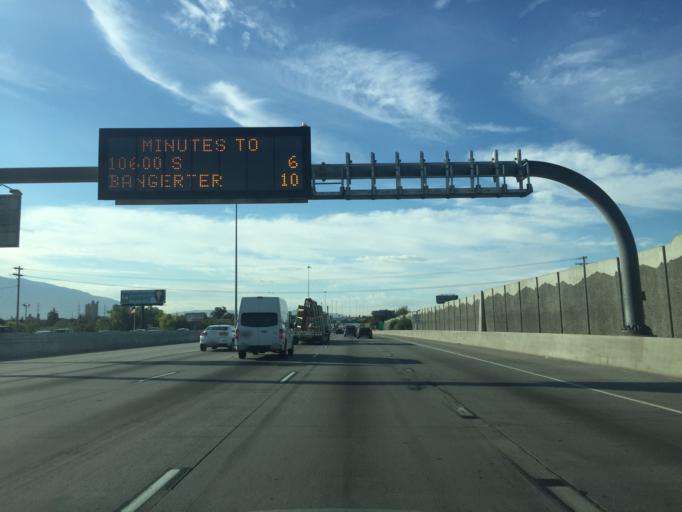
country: US
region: Utah
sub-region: Salt Lake County
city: Murray
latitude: 40.6671
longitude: -111.9018
